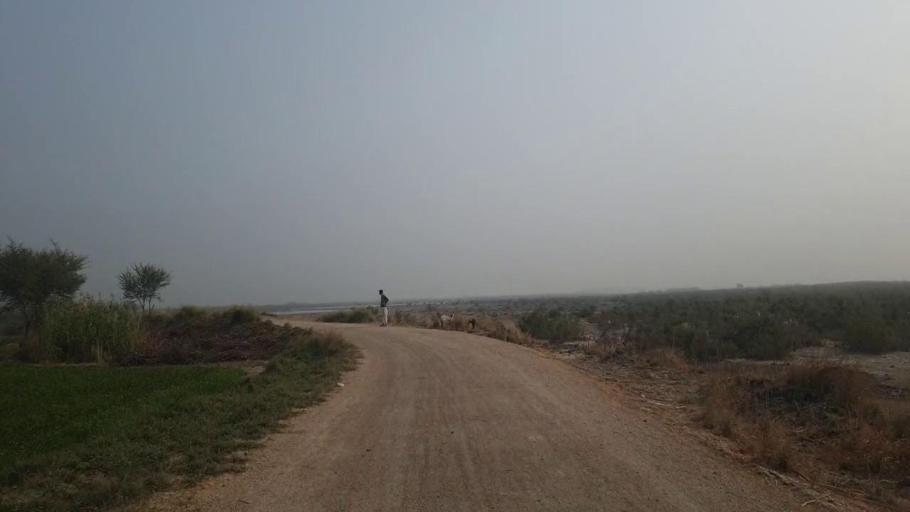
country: PK
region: Sindh
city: Tando Adam
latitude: 25.8296
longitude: 68.5978
